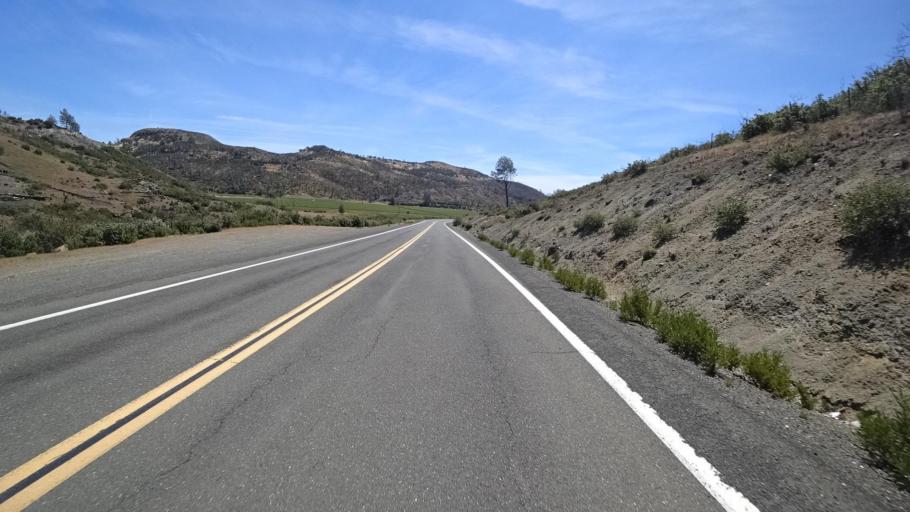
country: US
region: California
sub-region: Lake County
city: Hidden Valley Lake
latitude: 38.7315
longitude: -122.5234
